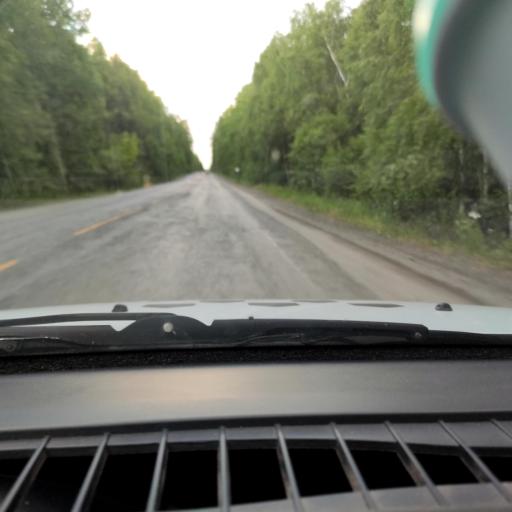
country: RU
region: Chelyabinsk
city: Karabash
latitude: 55.5339
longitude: 60.3444
